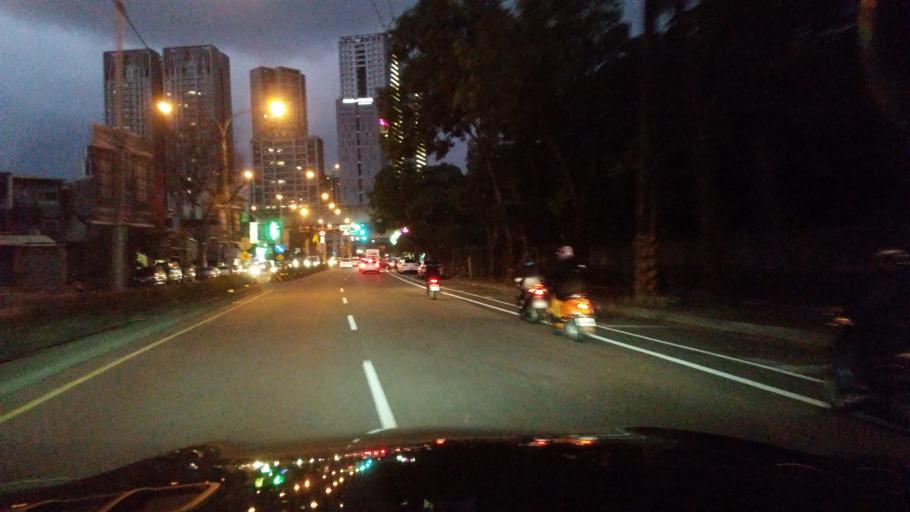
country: TW
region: Taiwan
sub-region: Taoyuan
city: Taoyuan
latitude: 25.0625
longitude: 121.3614
